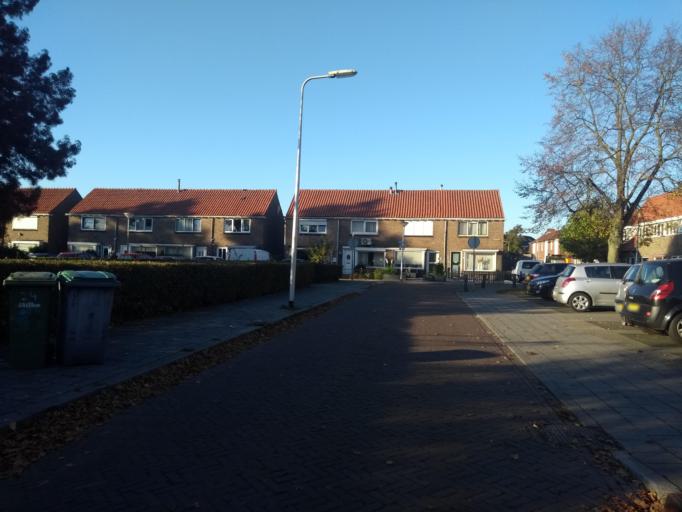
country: NL
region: Overijssel
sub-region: Gemeente Almelo
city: Almelo
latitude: 52.3484
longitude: 6.6582
